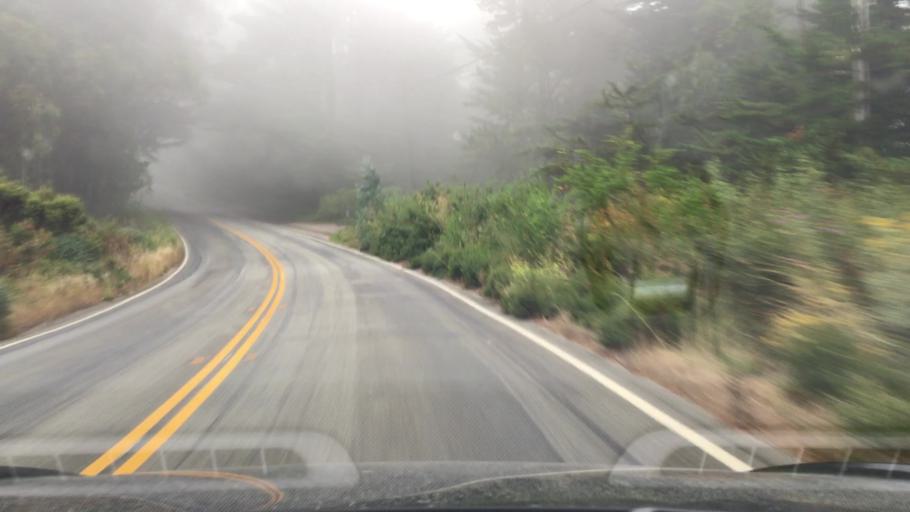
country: US
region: California
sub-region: San Mateo County
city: Highlands-Baywood Park
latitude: 37.4697
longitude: -122.3541
